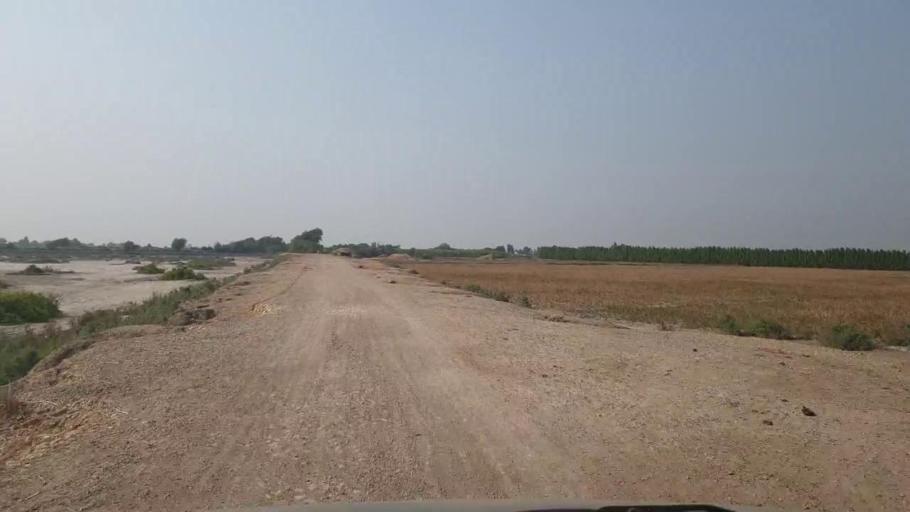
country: PK
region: Sindh
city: Tando Muhammad Khan
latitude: 25.0465
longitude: 68.3770
